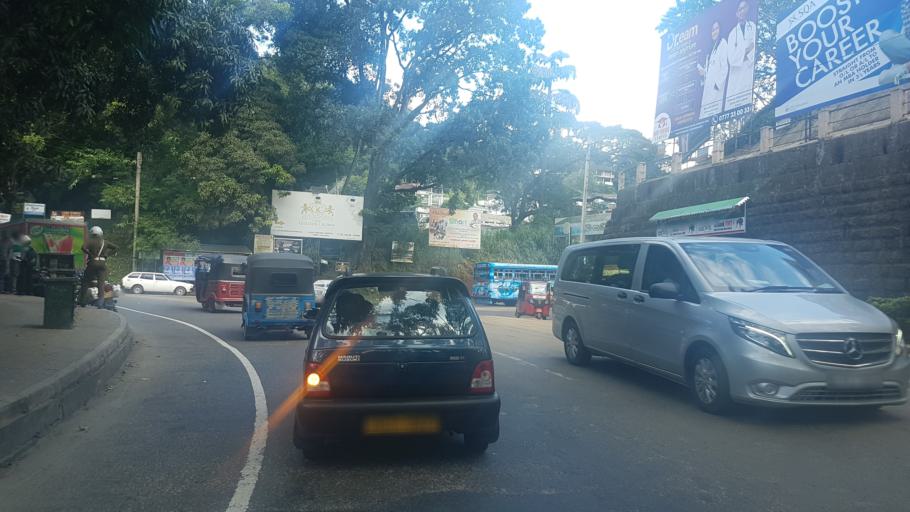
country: LK
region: Central
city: Kandy
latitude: 7.2869
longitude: 80.6474
